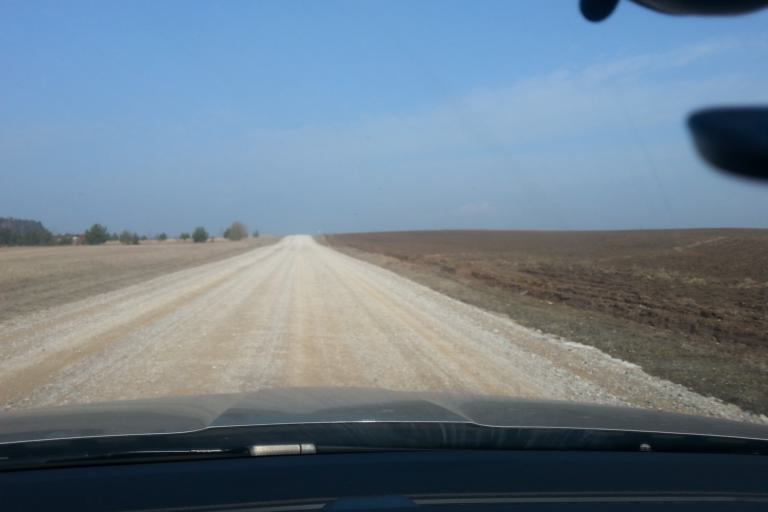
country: LT
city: Trakai
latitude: 54.5893
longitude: 24.9771
